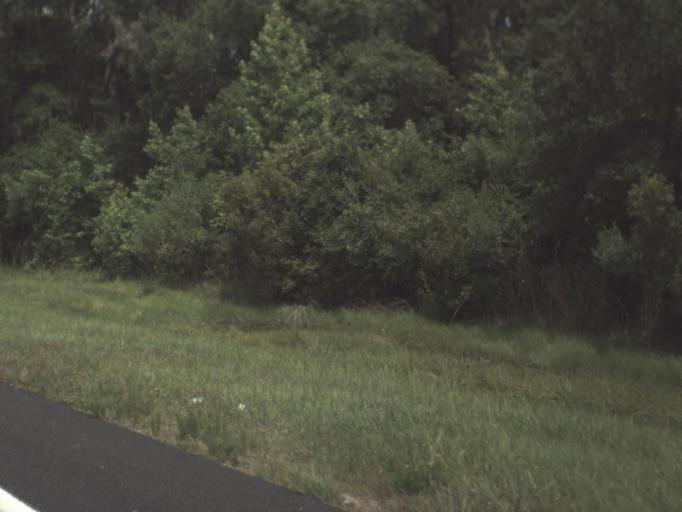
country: US
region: Florida
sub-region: Alachua County
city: Gainesville
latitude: 29.6089
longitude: -82.2358
